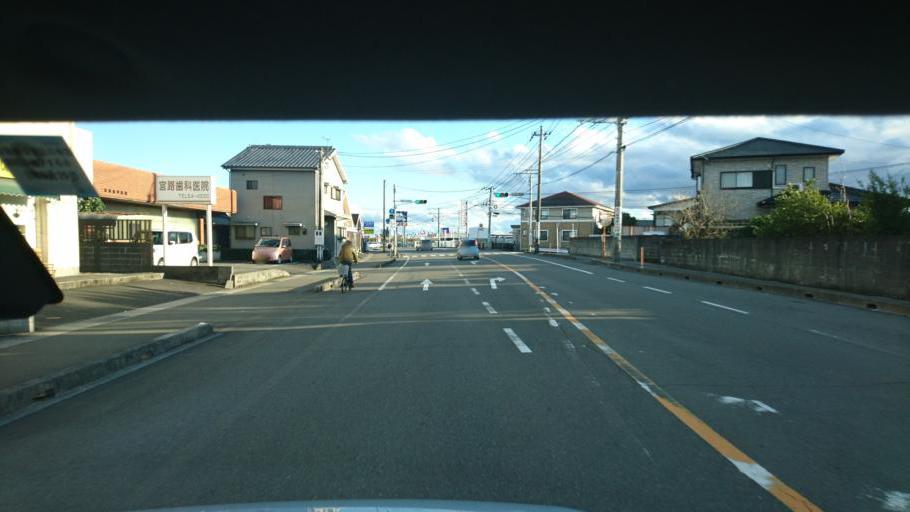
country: JP
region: Miyazaki
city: Miyazaki-shi
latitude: 31.8785
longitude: 131.4285
